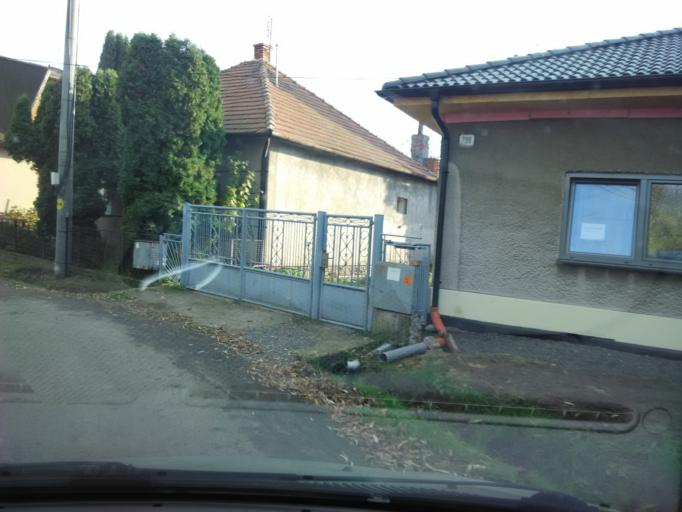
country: SK
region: Nitriansky
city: Tlmace
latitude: 48.3154
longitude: 18.5220
